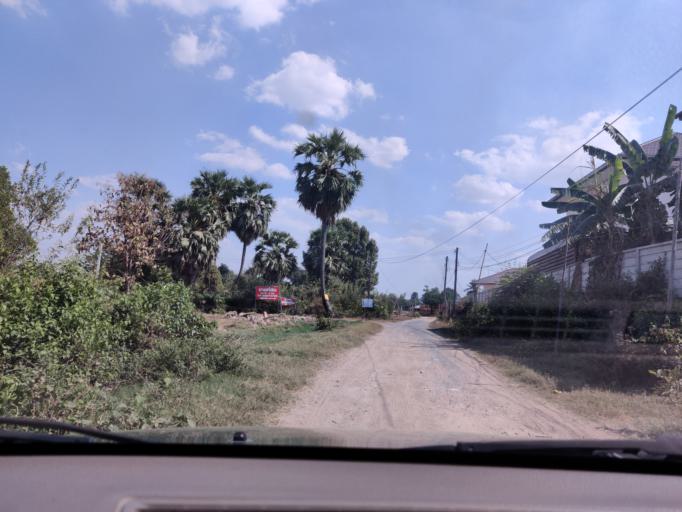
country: TH
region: Sisaket
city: Si Sa Ket
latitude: 15.1021
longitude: 104.3568
